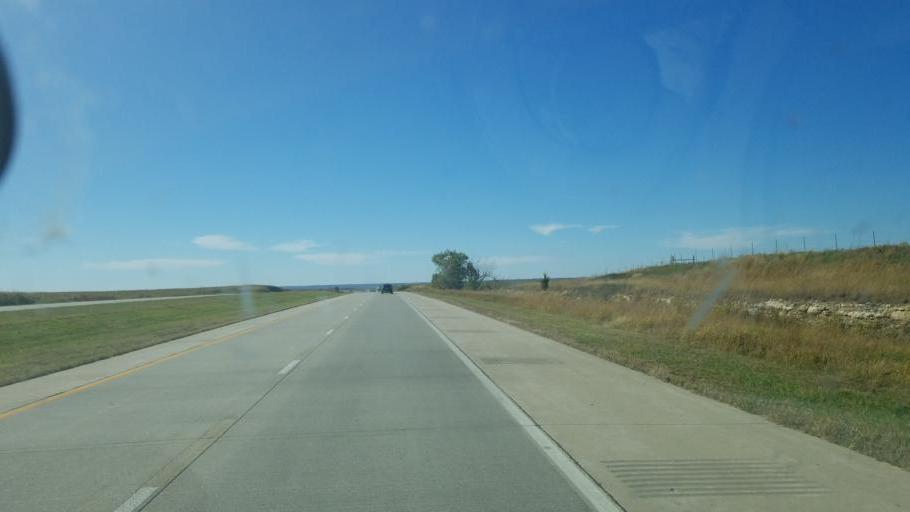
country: US
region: Kansas
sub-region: Riley County
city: Ogden
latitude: 39.0654
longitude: -96.6877
